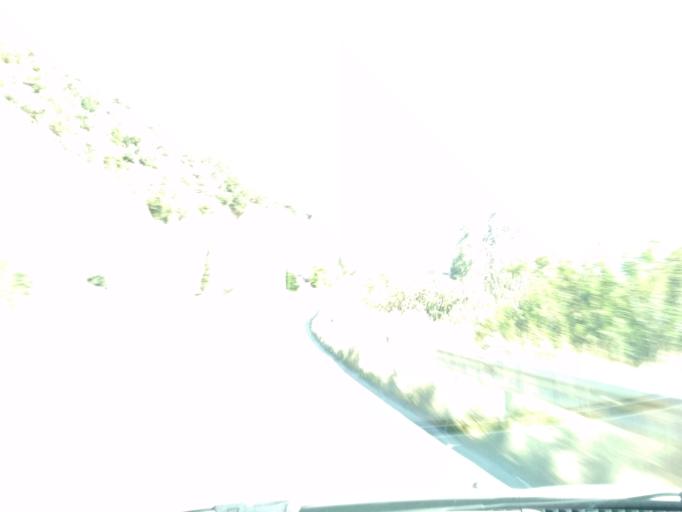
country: GR
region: Central Greece
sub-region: Nomos Evvoias
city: Oreoi
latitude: 38.8457
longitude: 23.0718
